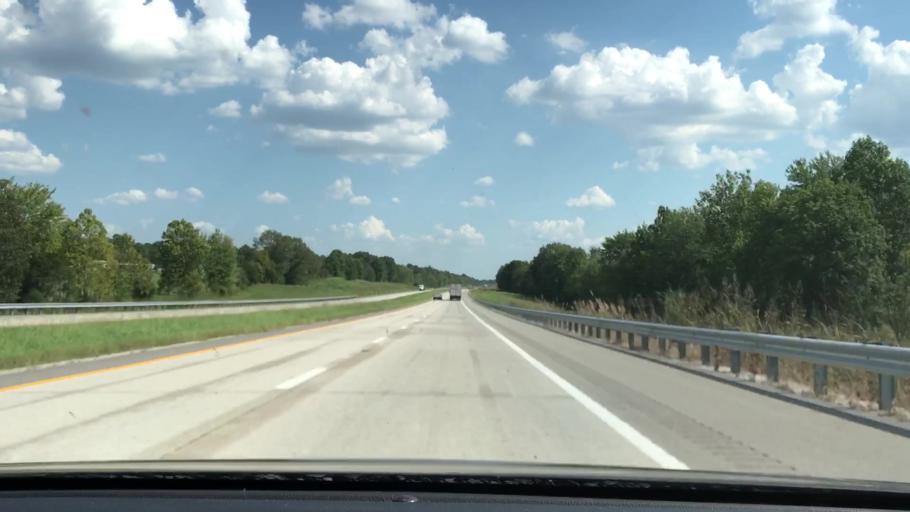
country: US
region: Kentucky
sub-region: Ohio County
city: Oak Grove
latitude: 37.3466
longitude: -86.7780
